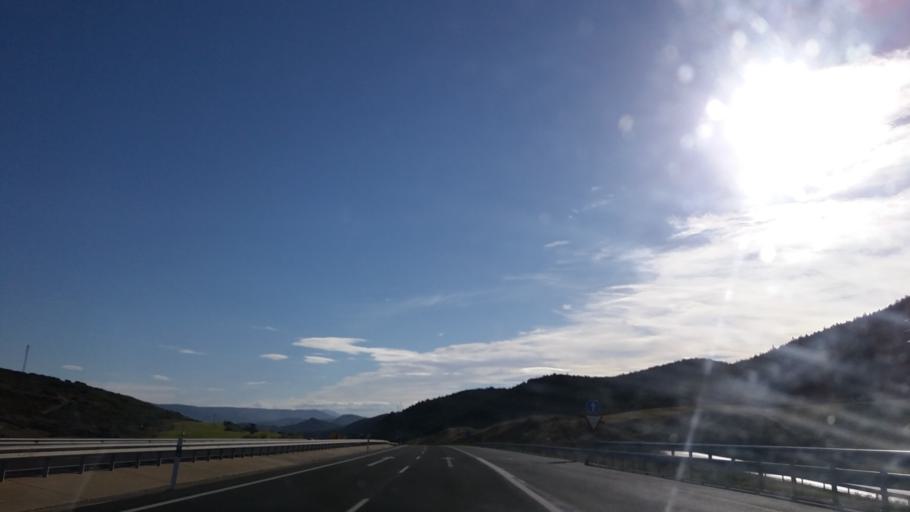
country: ES
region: Navarre
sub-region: Provincia de Navarra
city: Lumbier
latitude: 42.6313
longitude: -1.3236
